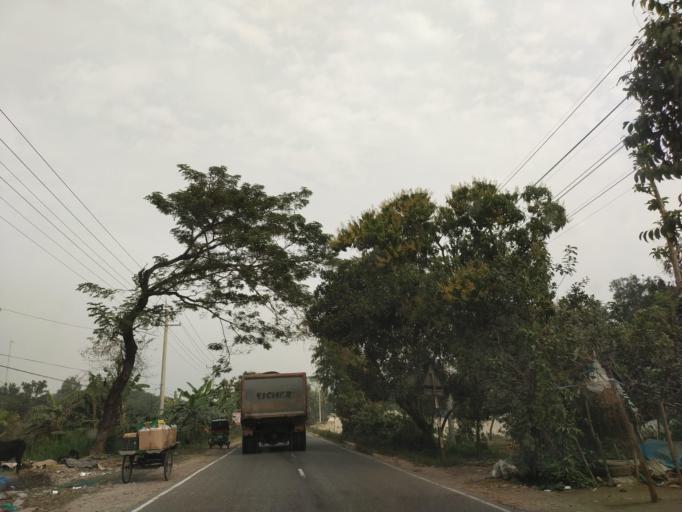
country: BD
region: Dhaka
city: Narsingdi
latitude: 24.0243
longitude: 90.7383
